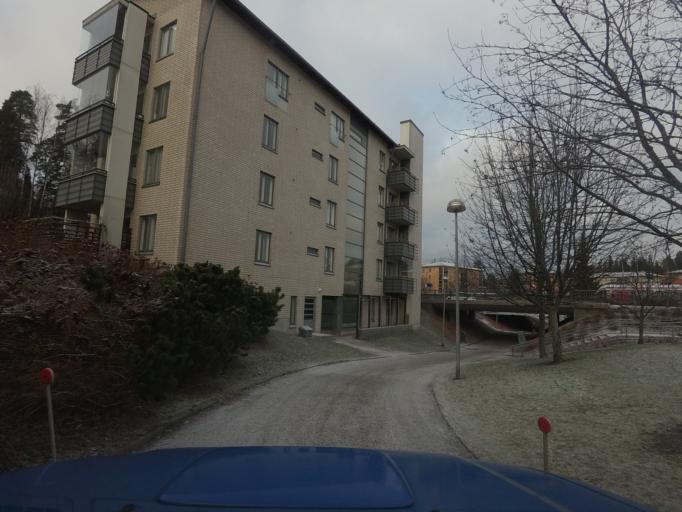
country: FI
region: Uusimaa
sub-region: Helsinki
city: Espoo
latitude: 60.2054
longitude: 24.6810
